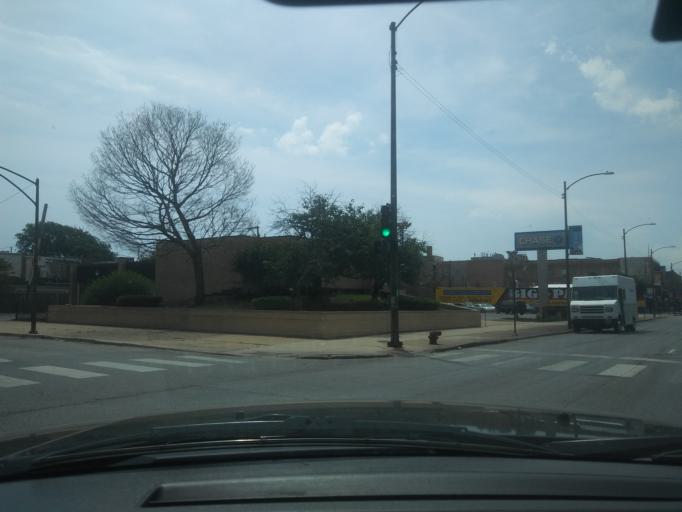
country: US
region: Illinois
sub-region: Cook County
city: Evergreen Park
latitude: 41.7811
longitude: -87.6837
